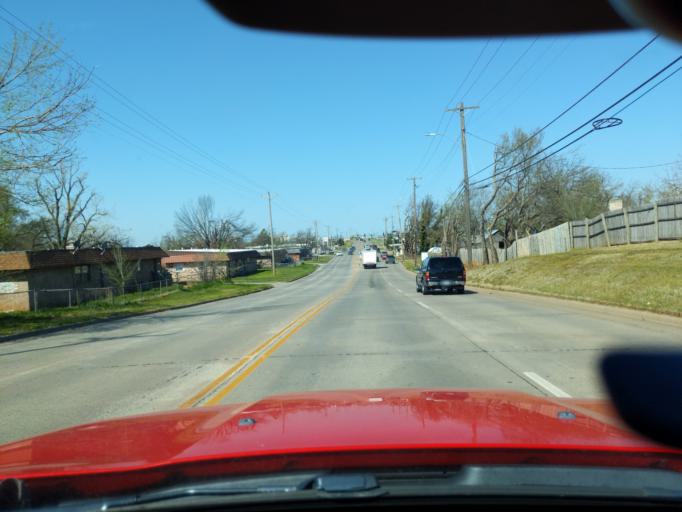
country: US
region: Oklahoma
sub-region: Cleveland County
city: Moore
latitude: 35.3489
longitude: -97.4876
